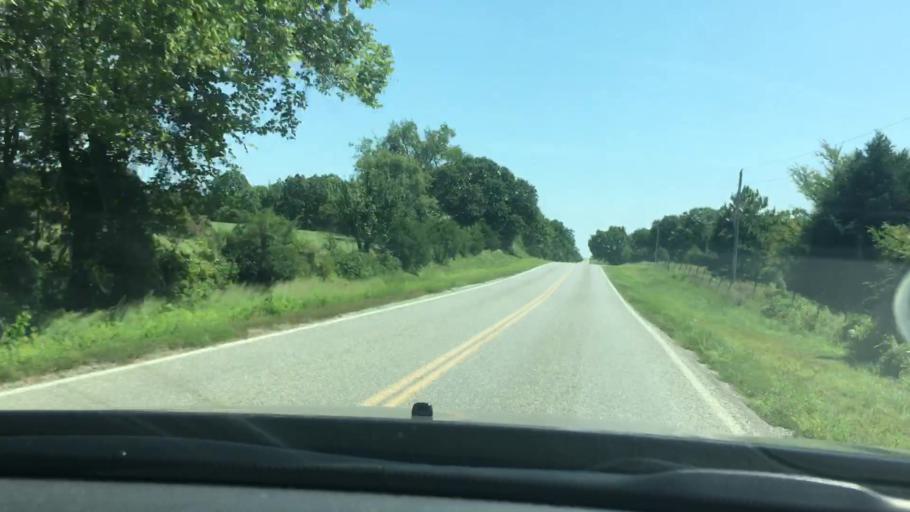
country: US
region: Oklahoma
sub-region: Johnston County
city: Tishomingo
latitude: 34.2742
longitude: -96.5349
